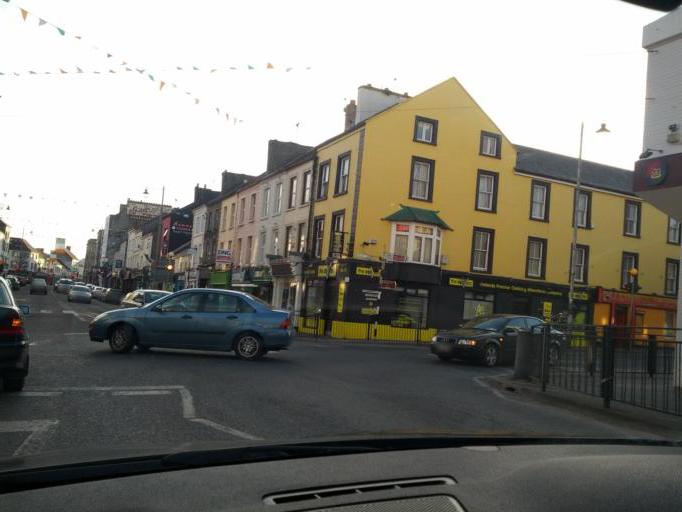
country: IE
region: Munster
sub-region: North Tipperary
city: Nenagh
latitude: 52.8640
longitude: -8.1979
